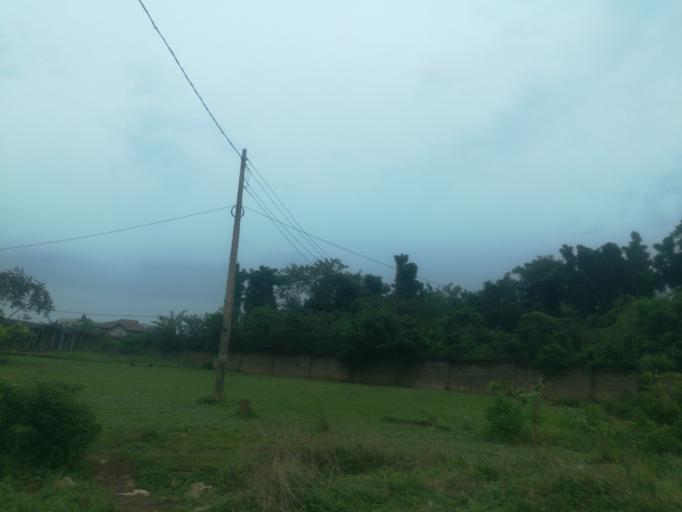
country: NG
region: Oyo
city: Ibadan
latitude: 7.3917
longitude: 3.9647
